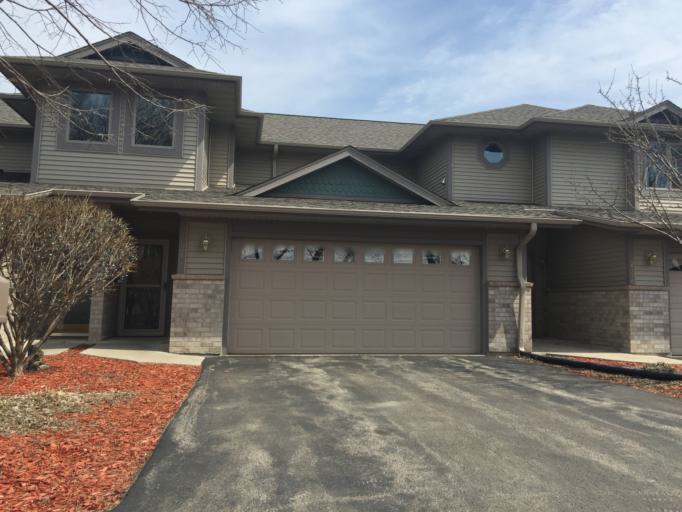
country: US
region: Michigan
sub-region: Menominee County
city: Menominee
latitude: 45.1183
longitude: -87.6128
